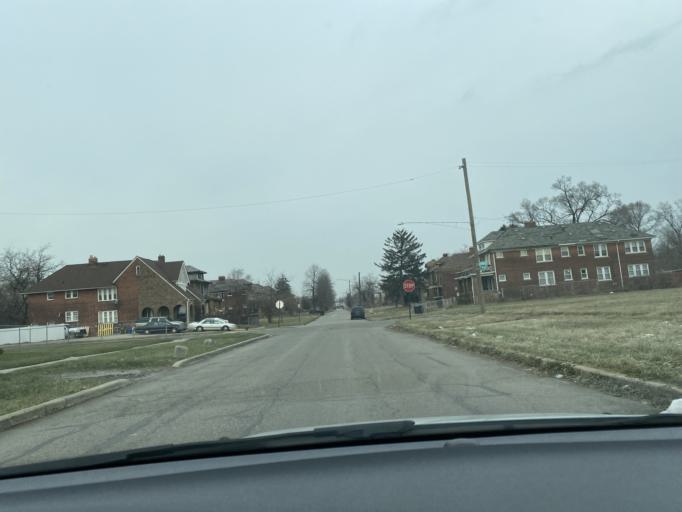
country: US
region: Michigan
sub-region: Wayne County
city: Highland Park
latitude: 42.3698
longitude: -83.1258
